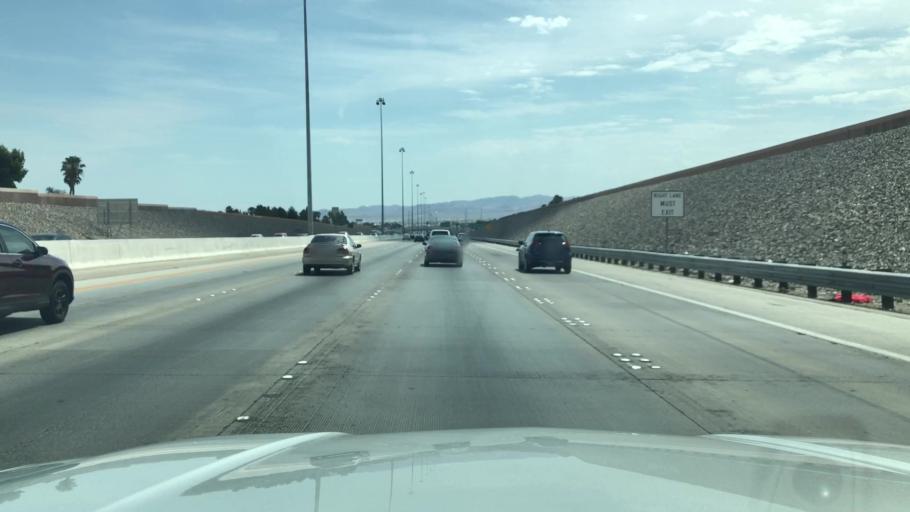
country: US
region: Nevada
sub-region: Clark County
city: Whitney
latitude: 36.0260
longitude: -115.0732
